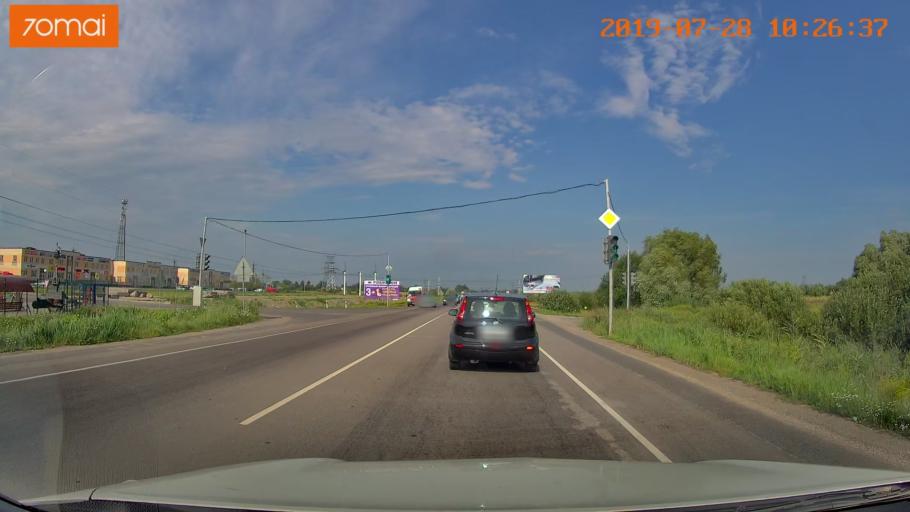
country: RU
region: Kaliningrad
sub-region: Gorod Kaliningrad
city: Kaliningrad
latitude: 54.7689
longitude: 20.5295
